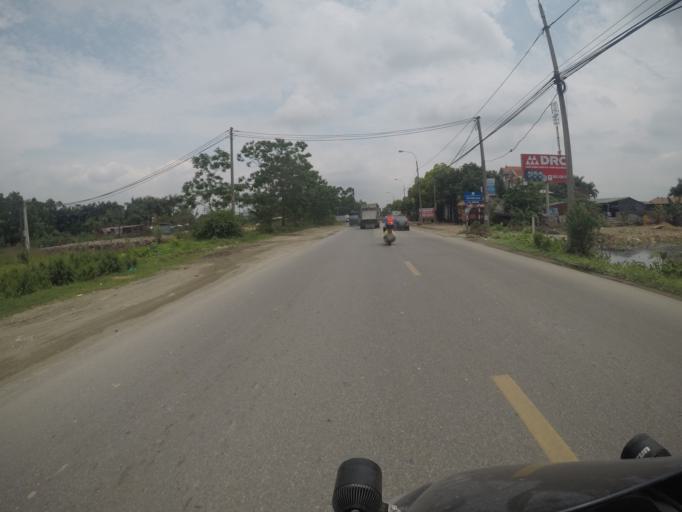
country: VN
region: Ha Noi
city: Soc Son
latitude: 21.2289
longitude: 105.8490
